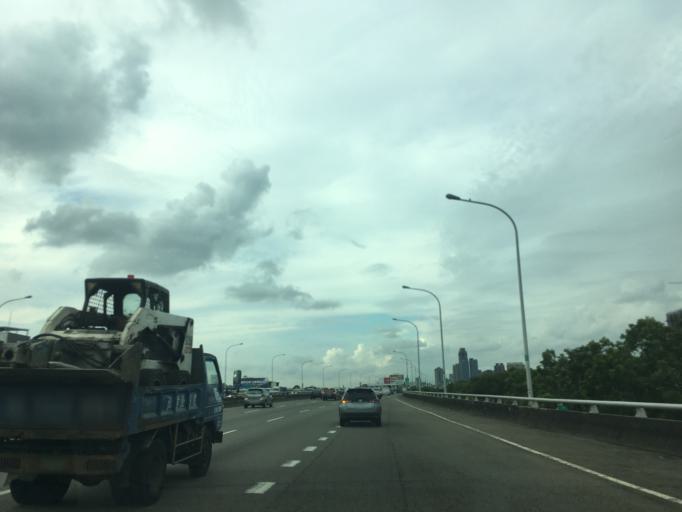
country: TW
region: Taiwan
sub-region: Taichung City
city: Taichung
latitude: 24.1533
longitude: 120.6243
